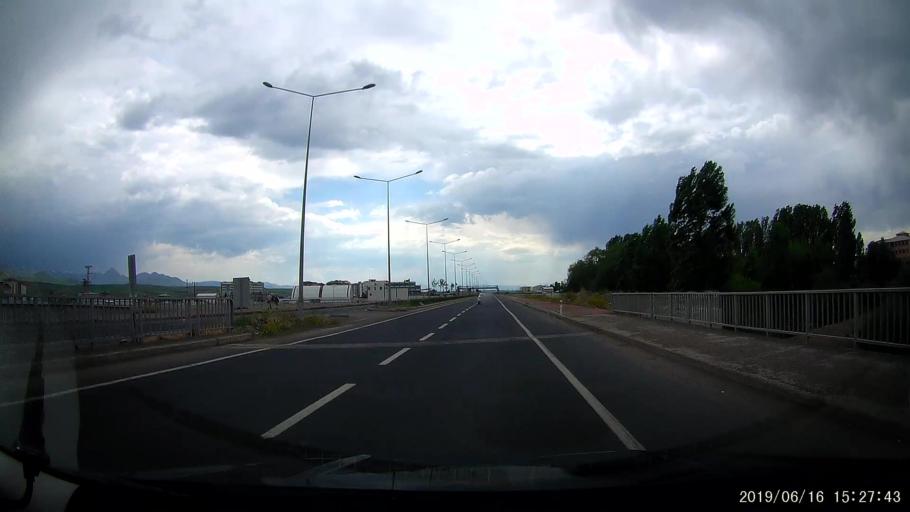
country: TR
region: Erzurum
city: Horasan
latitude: 40.0344
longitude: 42.1538
